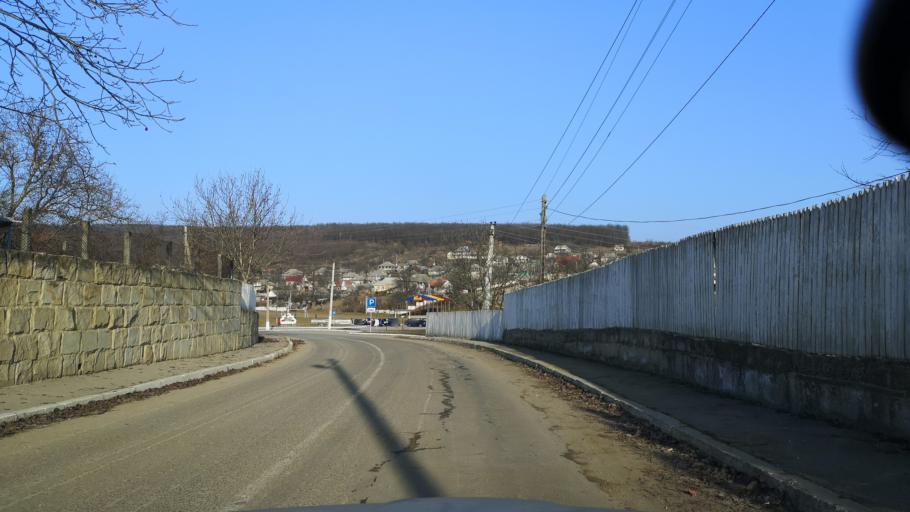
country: MD
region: Stinga Nistrului
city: Bucovat
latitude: 47.1159
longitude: 28.5074
